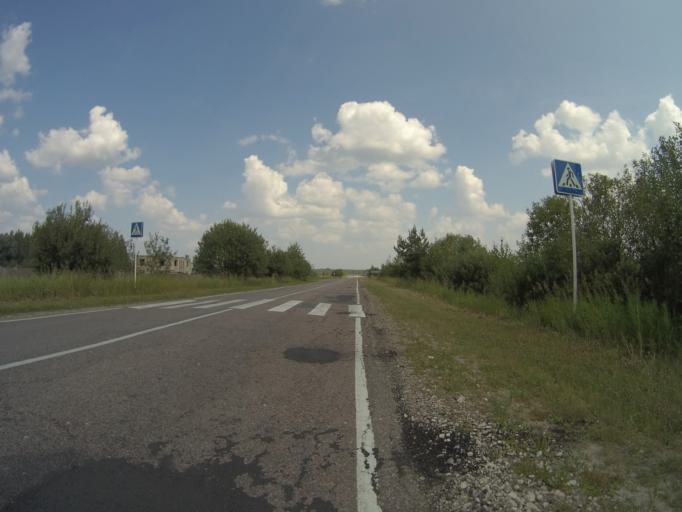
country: RU
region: Vladimir
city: Anopino
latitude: 55.6367
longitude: 40.8146
